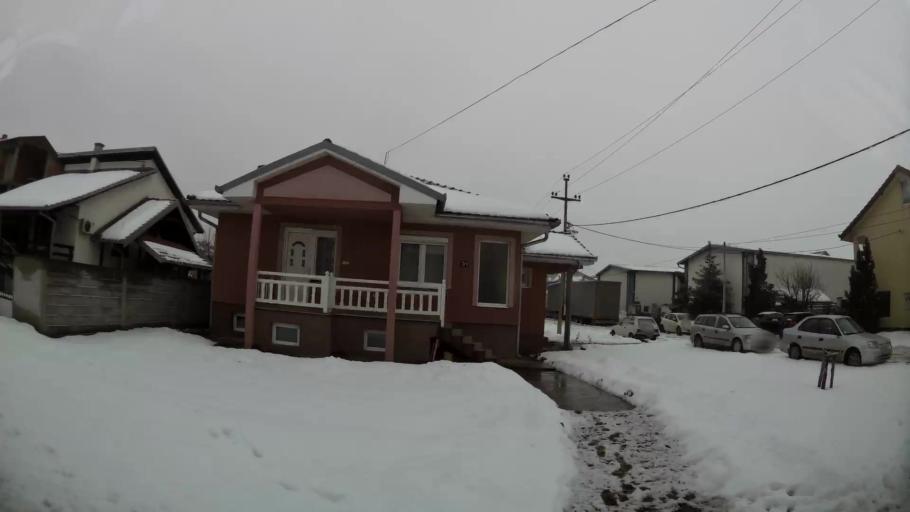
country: RS
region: Central Serbia
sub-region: Belgrade
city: Surcin
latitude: 44.8743
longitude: 20.3153
